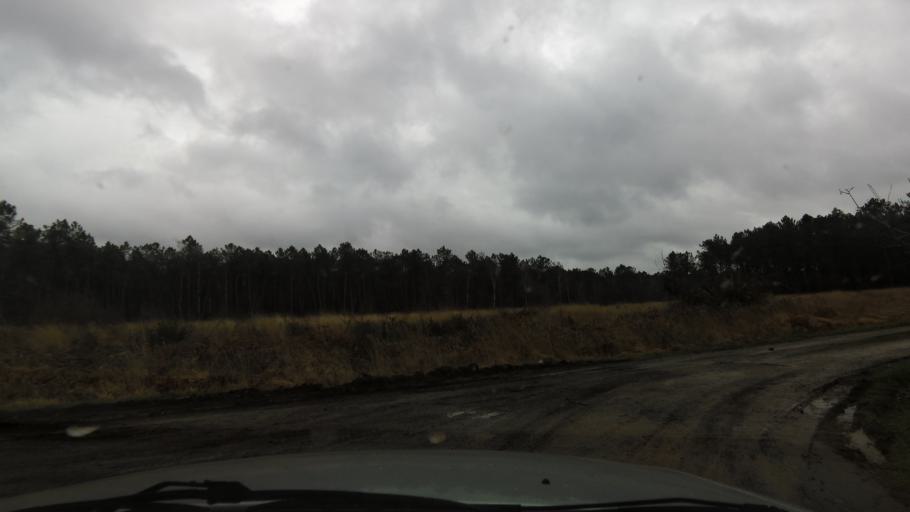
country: FR
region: Brittany
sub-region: Departement du Morbihan
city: Molac
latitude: 47.7661
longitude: -2.4792
